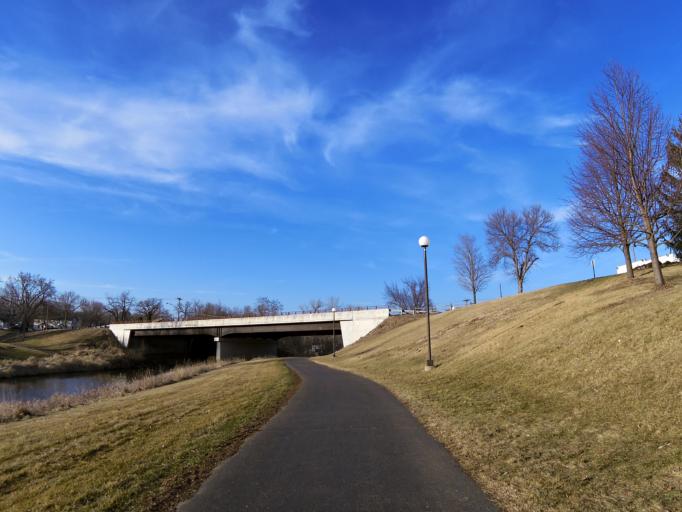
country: US
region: Minnesota
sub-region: Goodhue County
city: Cannon Falls
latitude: 44.5073
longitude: -92.9077
